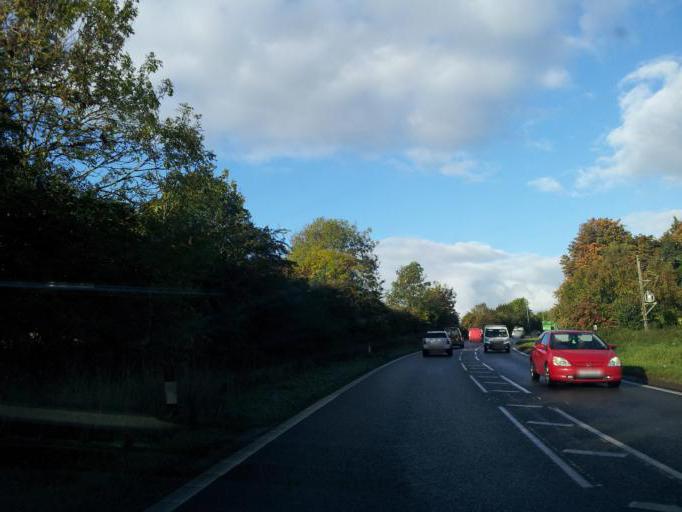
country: GB
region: England
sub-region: Norfolk
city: Hethersett
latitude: 52.6570
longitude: 1.1257
